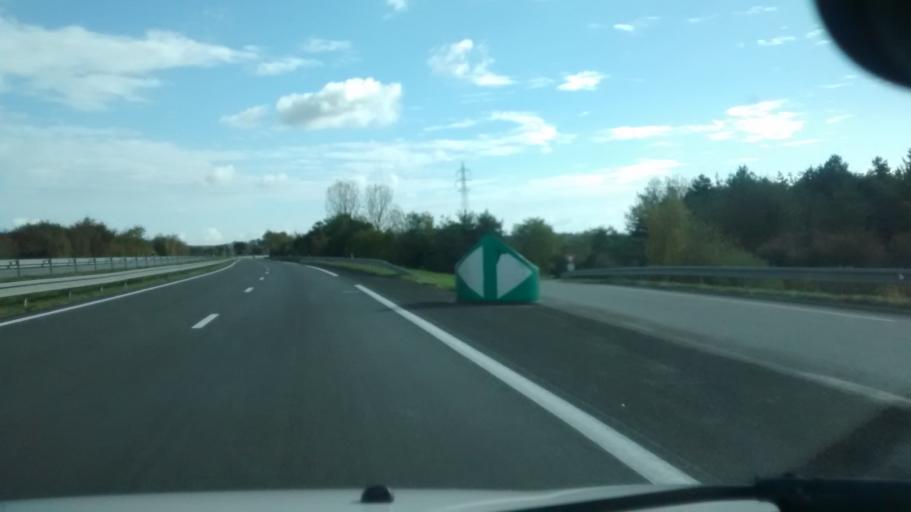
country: FR
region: Pays de la Loire
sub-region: Departement de Maine-et-Loire
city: Pouance
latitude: 47.7570
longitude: -1.1735
